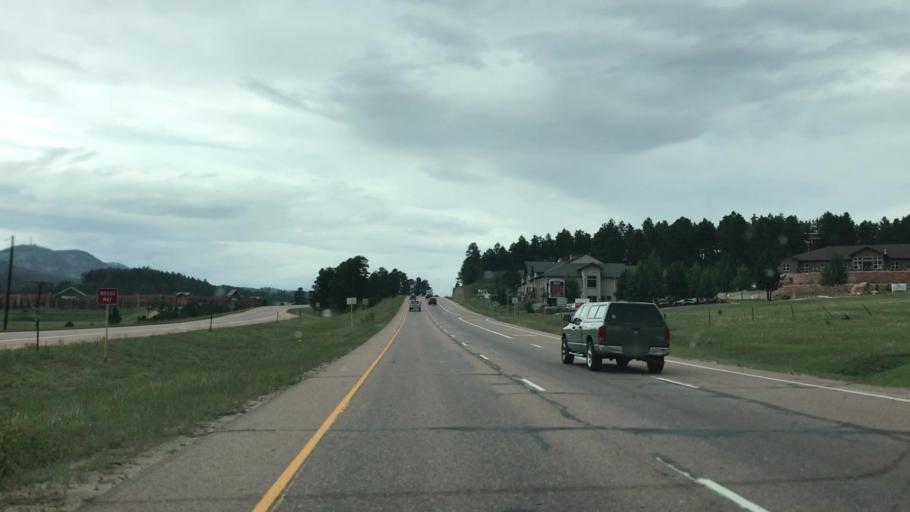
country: US
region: Colorado
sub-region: Teller County
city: Woodland Park
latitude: 38.9671
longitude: -105.0336
